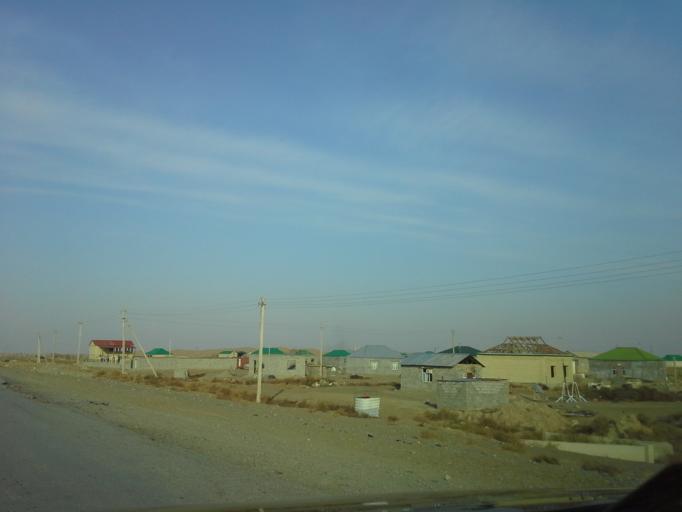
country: TM
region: Ahal
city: Abadan
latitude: 38.1814
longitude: 58.0407
